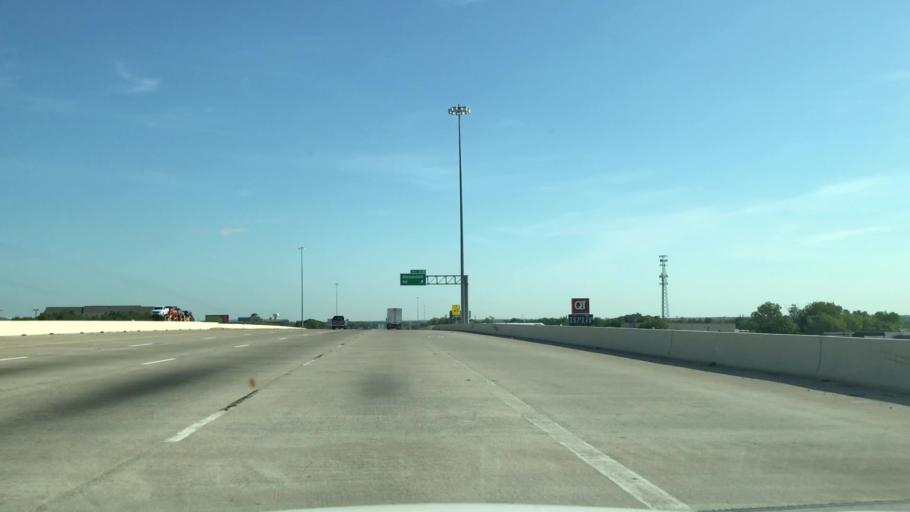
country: US
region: Texas
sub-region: Collin County
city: McKinney
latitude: 33.2288
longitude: -96.6329
